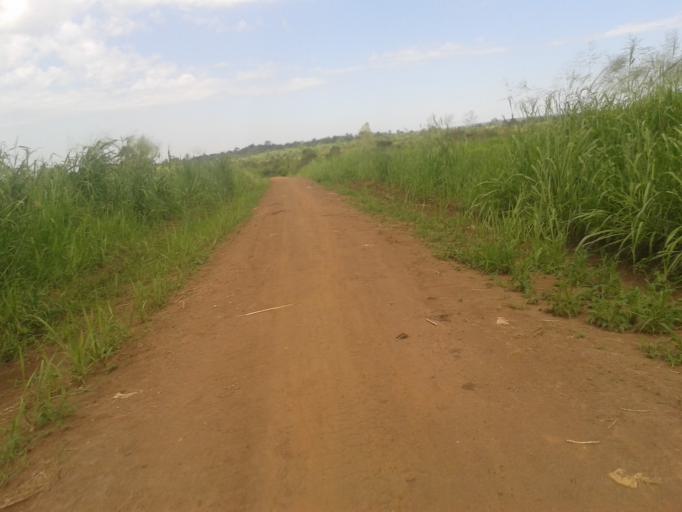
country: UG
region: Northern Region
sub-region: Gulu District
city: Gulu
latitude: 2.8237
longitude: 32.2619
